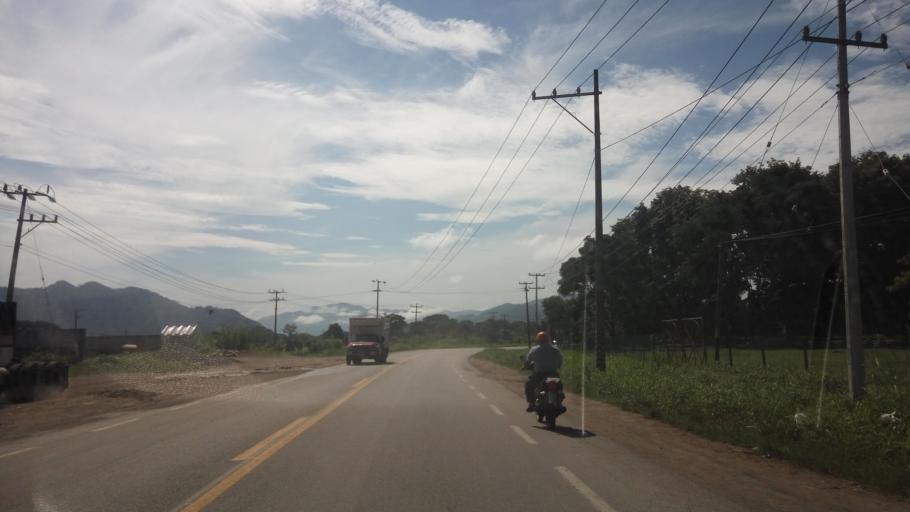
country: MX
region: Tabasco
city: Teapa
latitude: 17.5782
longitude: -92.9608
